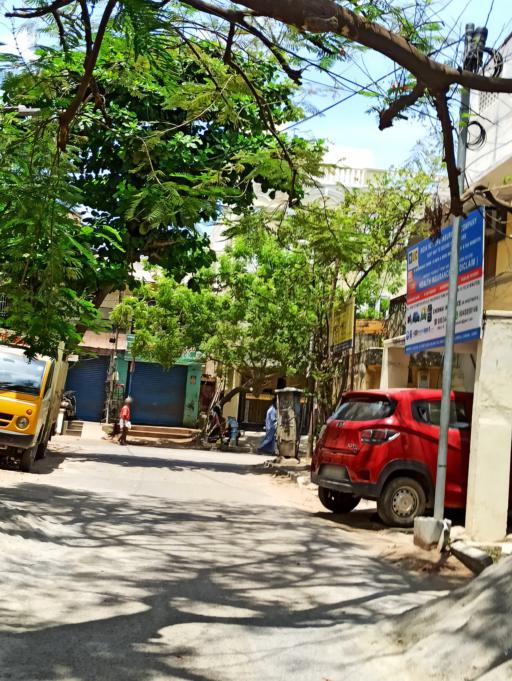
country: IN
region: Tamil Nadu
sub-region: Chennai
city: Chetput
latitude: 13.0605
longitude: 80.2229
